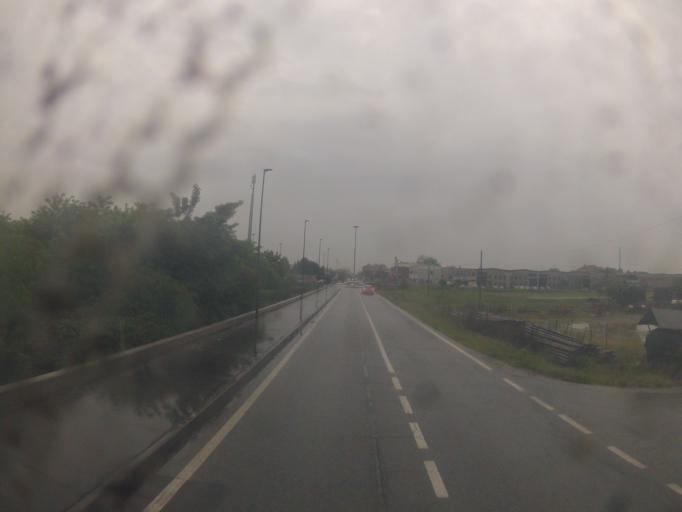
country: IT
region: Piedmont
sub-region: Provincia di Torino
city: La Loggia
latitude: 44.9451
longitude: 7.6698
